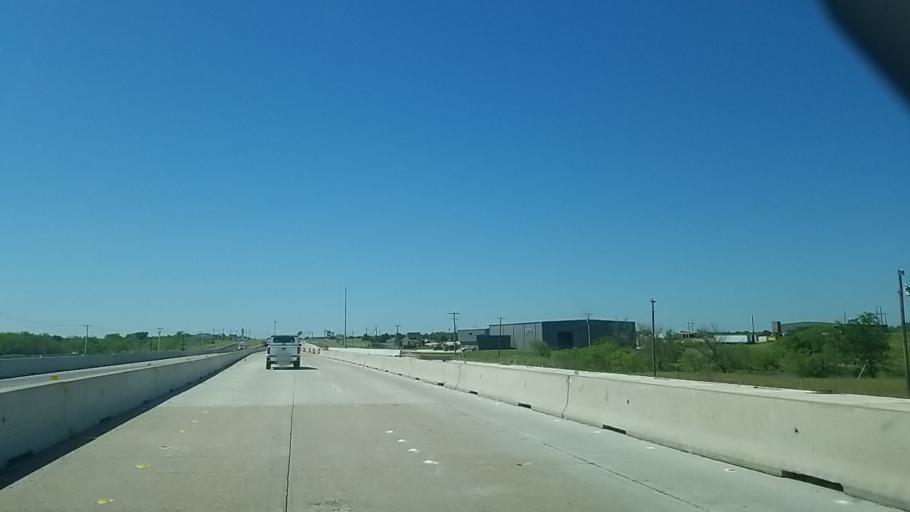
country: US
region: Texas
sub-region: Navarro County
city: Corsicana
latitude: 32.0489
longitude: -96.4488
